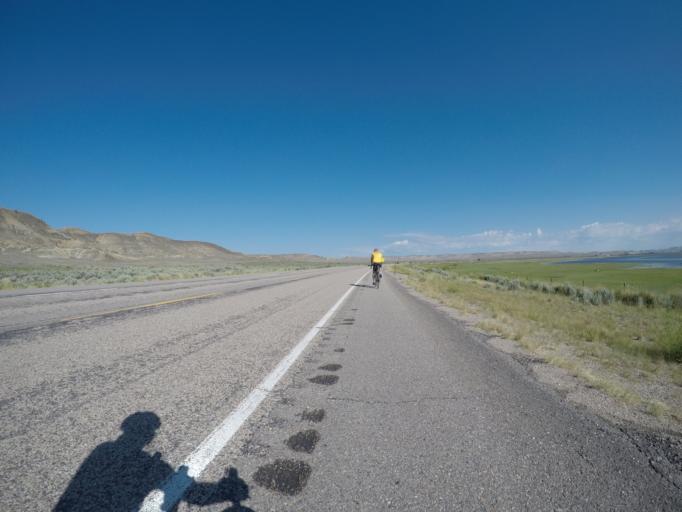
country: US
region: Wyoming
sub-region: Sublette County
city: Marbleton
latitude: 42.1217
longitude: -110.1837
